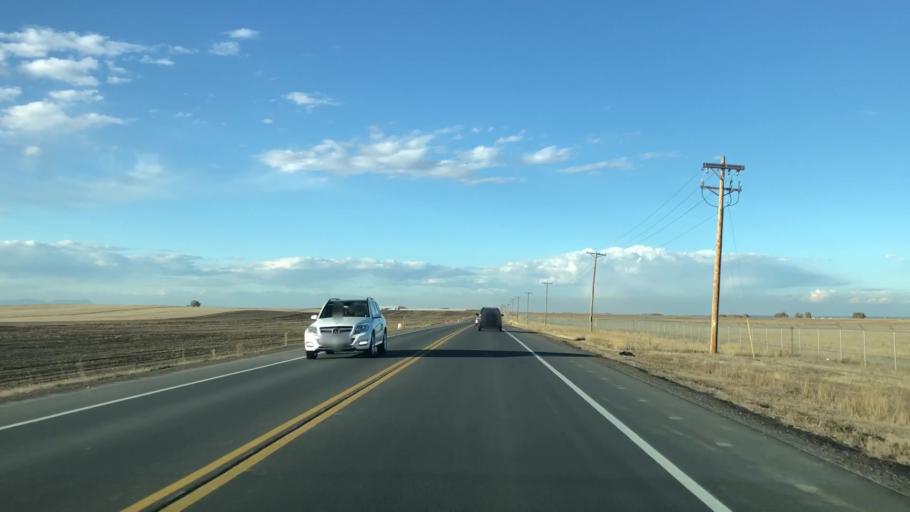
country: US
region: Colorado
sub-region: Larimer County
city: Loveland
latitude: 40.4475
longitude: -105.0204
